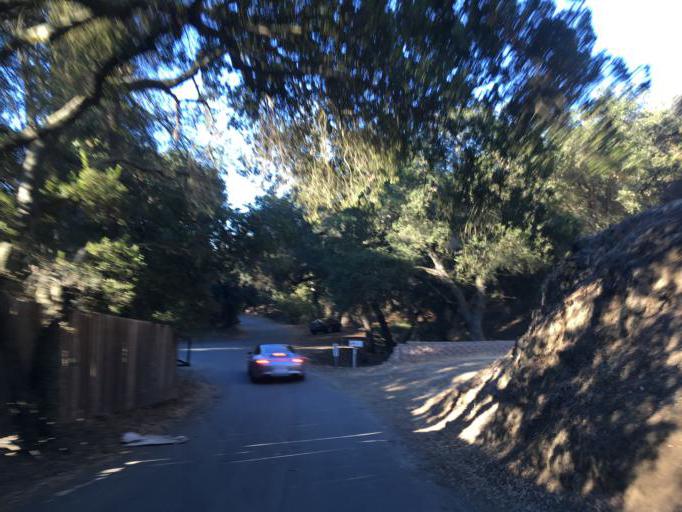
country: US
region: California
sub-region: Los Angeles County
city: Westlake Village
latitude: 34.0903
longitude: -118.8182
